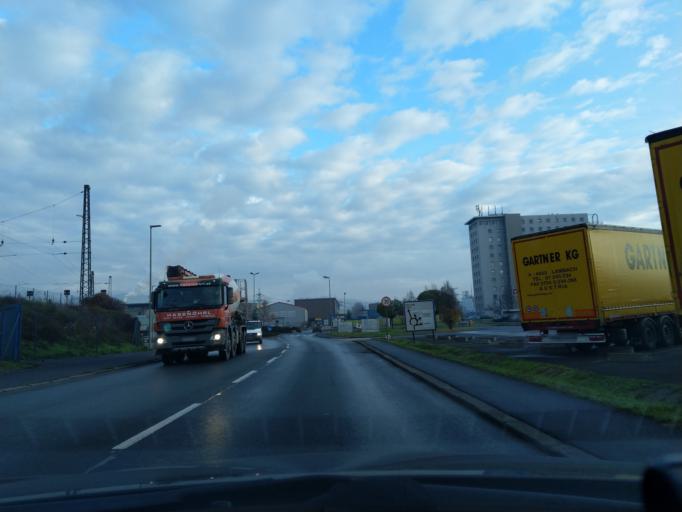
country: AT
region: Upper Austria
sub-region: Politischer Bezirk Urfahr-Umgebung
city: Steyregg
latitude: 48.2638
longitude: 14.3388
